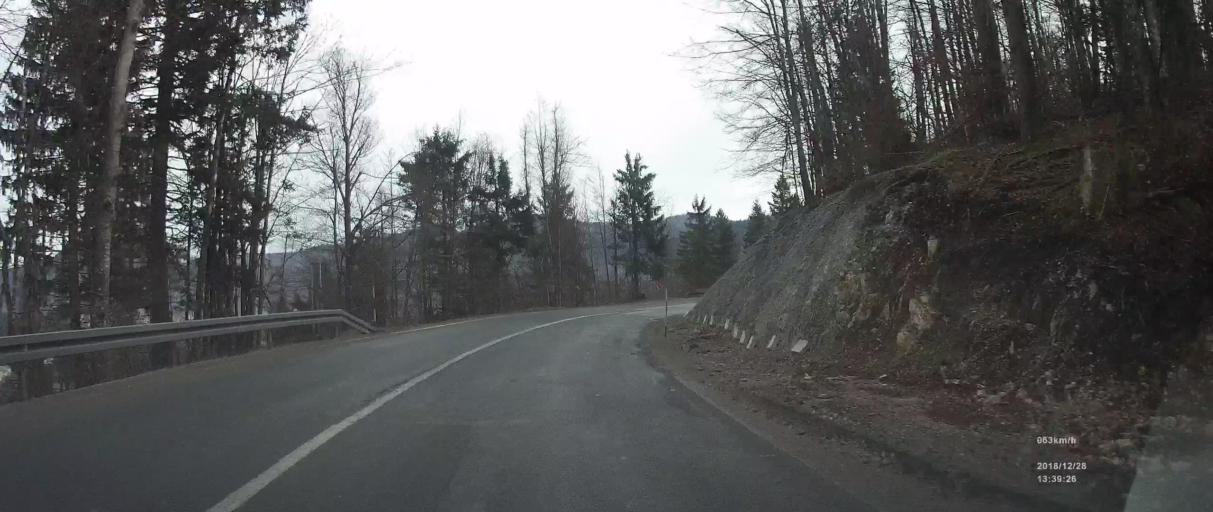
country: HR
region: Primorsko-Goranska
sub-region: Grad Delnice
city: Delnice
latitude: 45.3519
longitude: 14.7369
